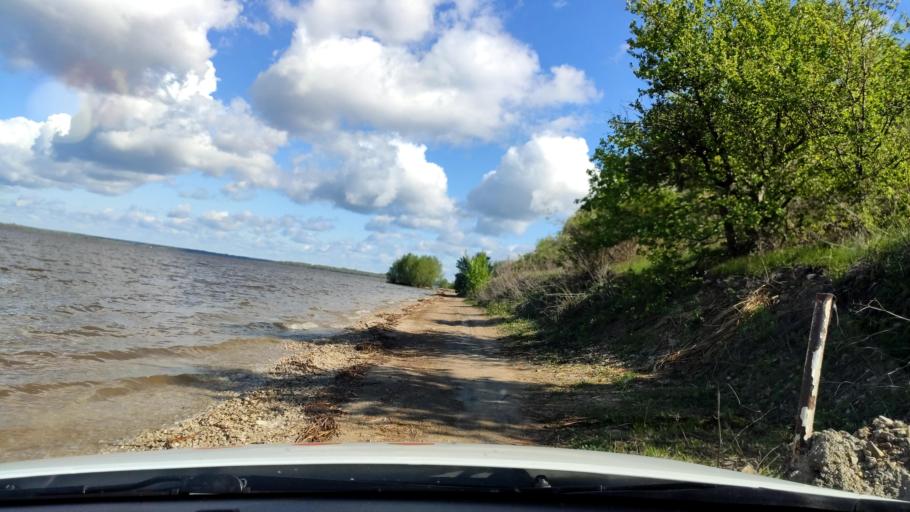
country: RU
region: Tatarstan
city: Sviyazhsk
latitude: 55.7658
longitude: 48.6855
